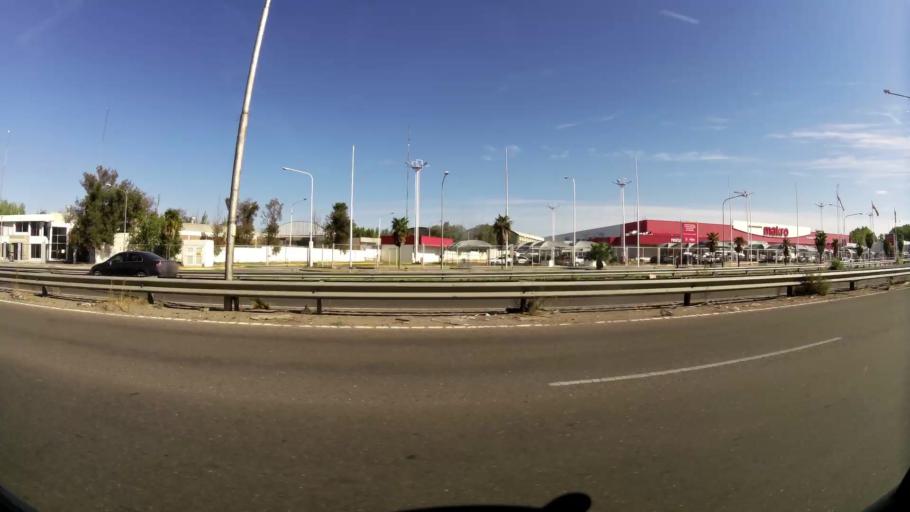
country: AR
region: Mendoza
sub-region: Departamento de Godoy Cruz
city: Godoy Cruz
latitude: -32.9255
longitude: -68.8294
